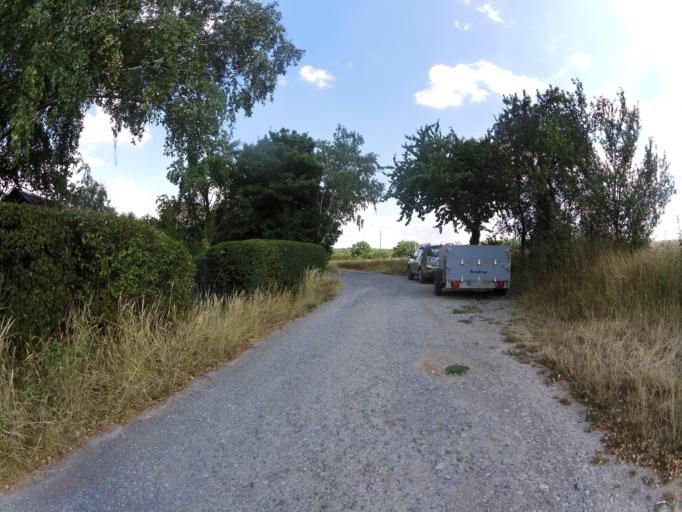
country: DE
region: Bavaria
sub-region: Regierungsbezirk Unterfranken
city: Ochsenfurt
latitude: 49.6594
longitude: 10.0659
